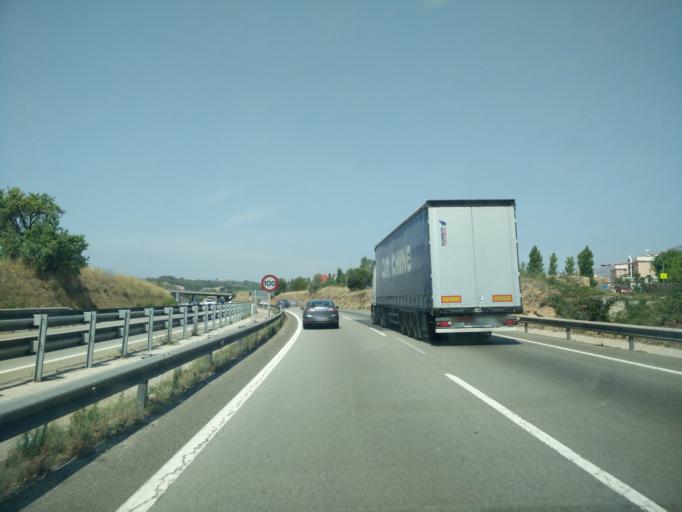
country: ES
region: Catalonia
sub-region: Provincia de Barcelona
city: Esparreguera
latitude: 41.5306
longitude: 1.8766
